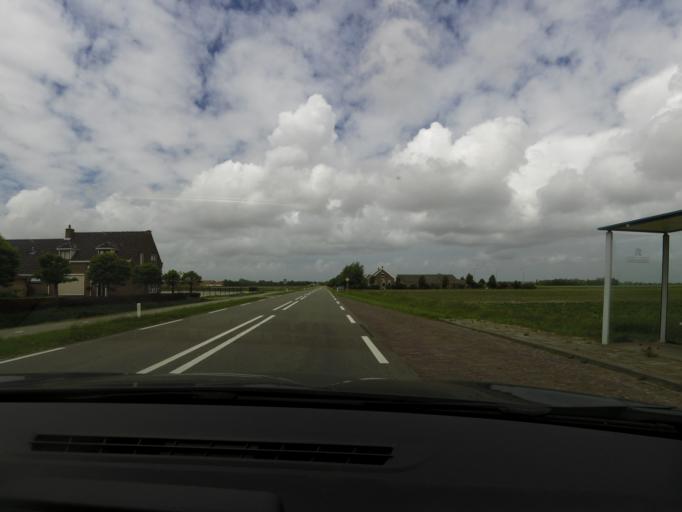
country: NL
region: Zeeland
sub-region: Schouwen-Duiveland
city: Scharendijke
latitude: 51.6846
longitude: 3.9418
